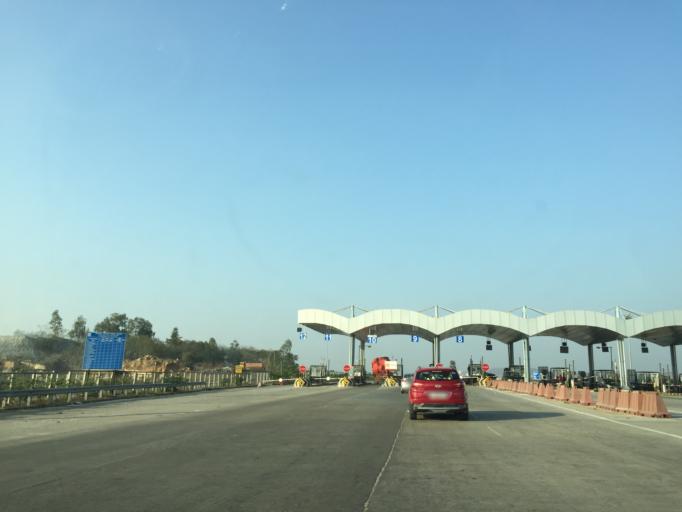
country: IN
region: Telangana
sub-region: Rangareddi
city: Ghatkesar
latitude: 17.4410
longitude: 78.6665
